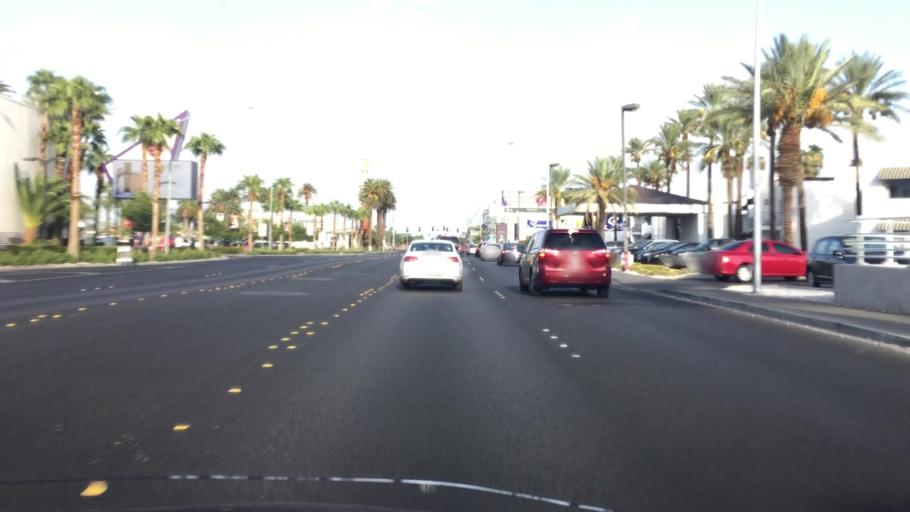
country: US
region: Nevada
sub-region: Clark County
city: Paradise
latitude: 36.1080
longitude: -115.1551
